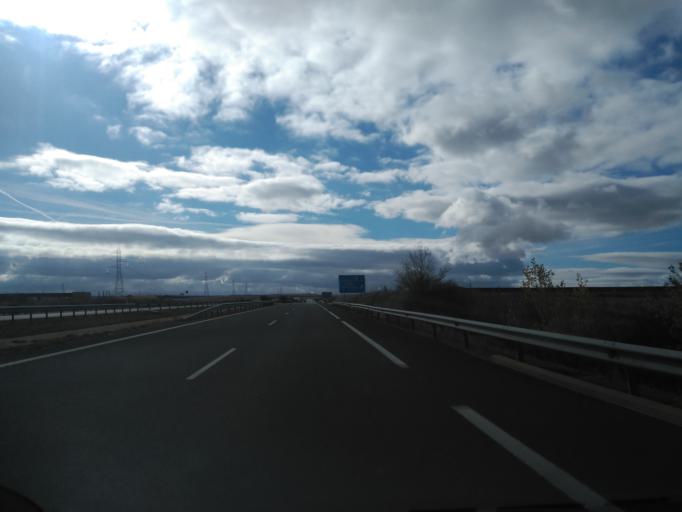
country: ES
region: Castille and Leon
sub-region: Provincia de Palencia
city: Abia de las Torres
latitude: 42.3767
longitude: -4.3875
